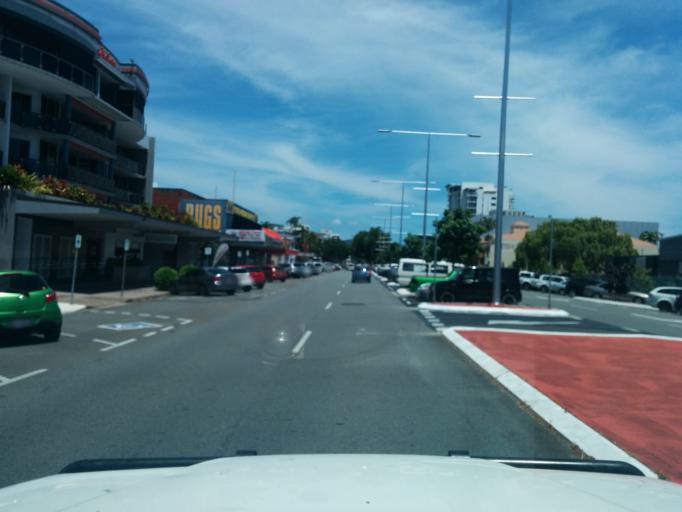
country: AU
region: Queensland
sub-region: Cairns
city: Cairns
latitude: -16.9197
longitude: 145.7721
